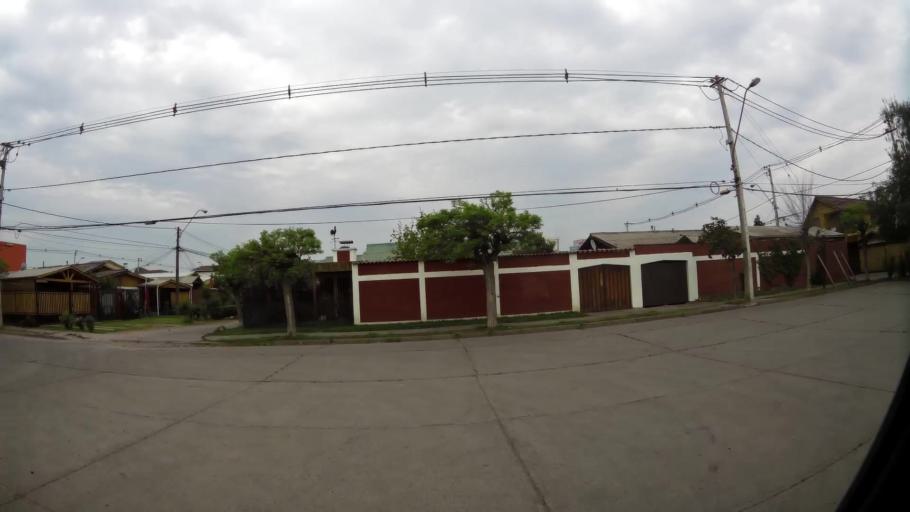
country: CL
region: Santiago Metropolitan
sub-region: Provincia de Santiago
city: Lo Prado
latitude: -33.4944
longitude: -70.7618
